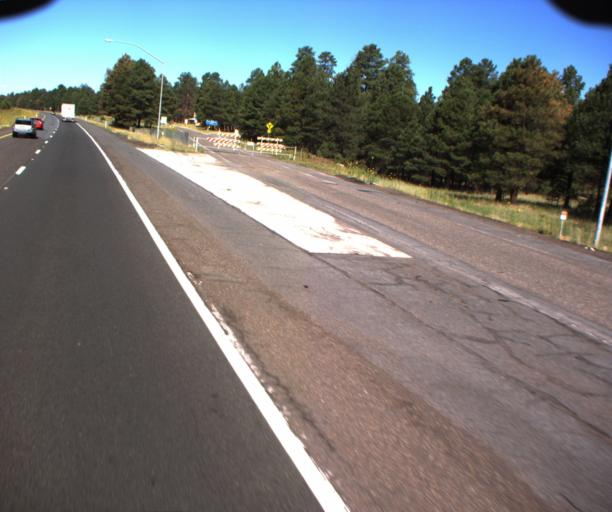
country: US
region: Arizona
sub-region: Coconino County
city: Parks
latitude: 35.2497
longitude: -111.8647
